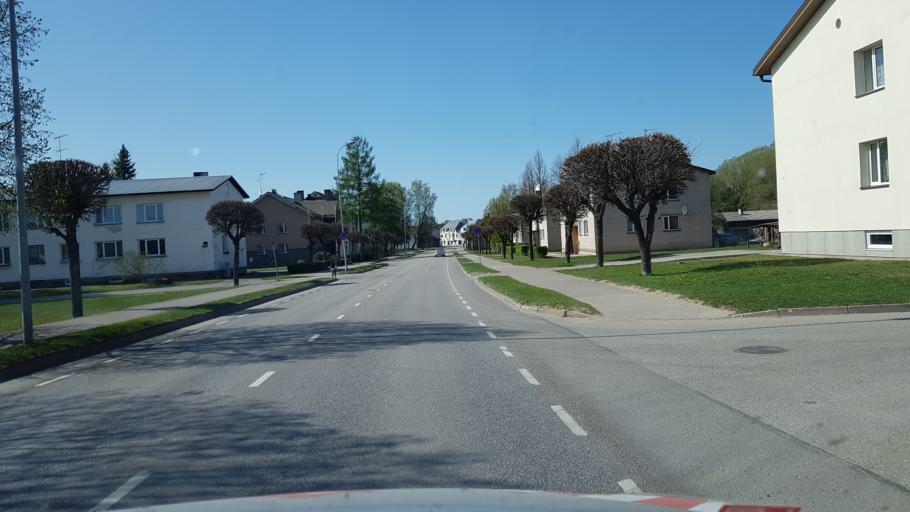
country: EE
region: Valgamaa
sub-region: Torva linn
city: Torva
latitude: 58.0006
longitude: 25.9277
